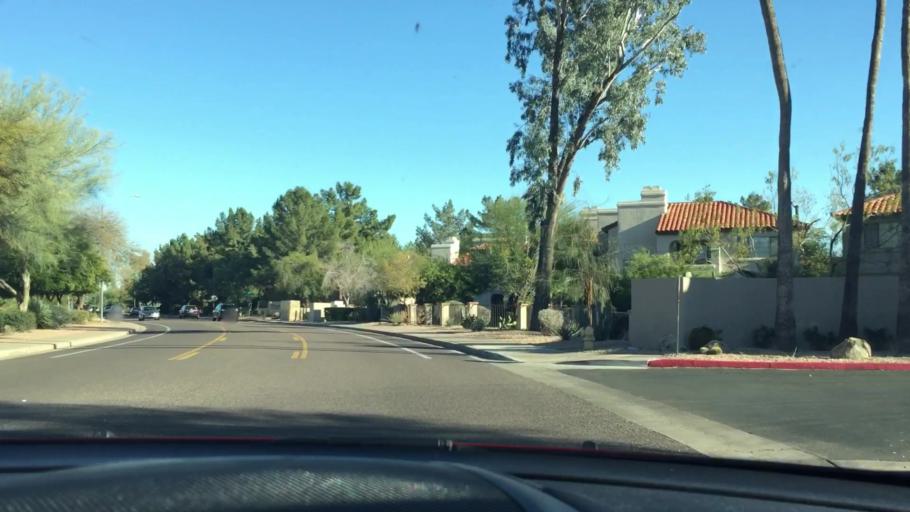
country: US
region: Arizona
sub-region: Maricopa County
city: Scottsdale
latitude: 33.5754
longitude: -111.8792
